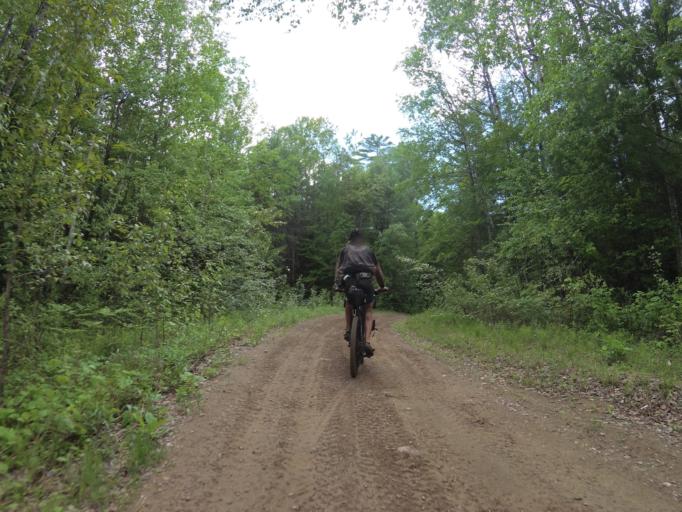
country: CA
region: Ontario
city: Renfrew
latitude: 45.1105
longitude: -76.8571
